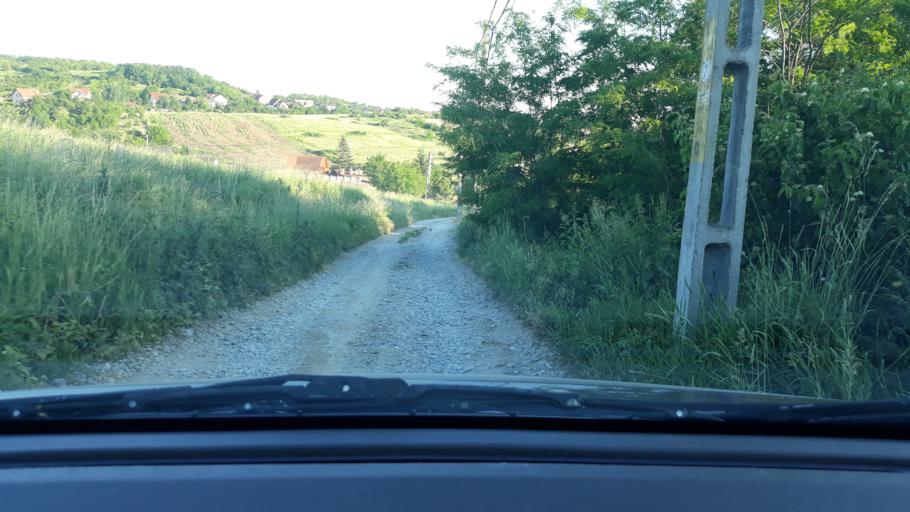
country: RO
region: Bihor
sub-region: Comuna Paleu
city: Paleu
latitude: 47.1001
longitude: 21.9348
